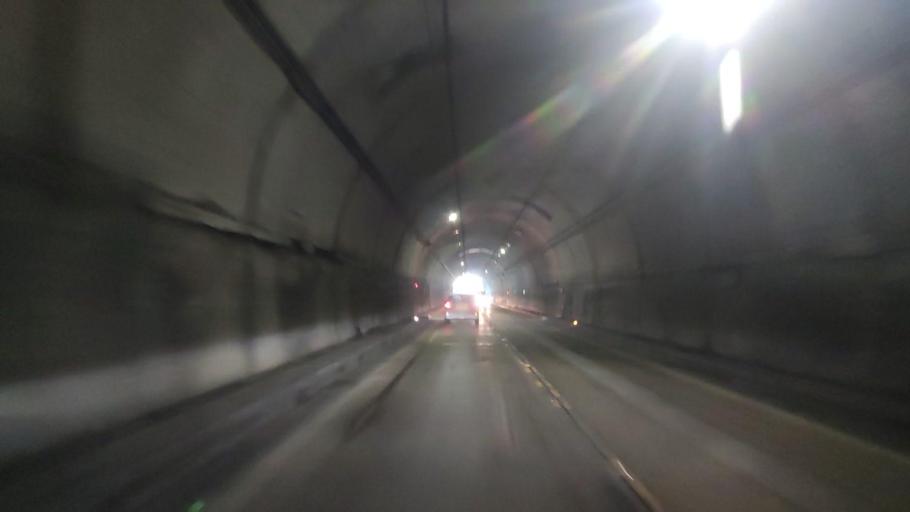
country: JP
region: Nara
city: Yoshino-cho
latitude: 34.3721
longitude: 135.9145
